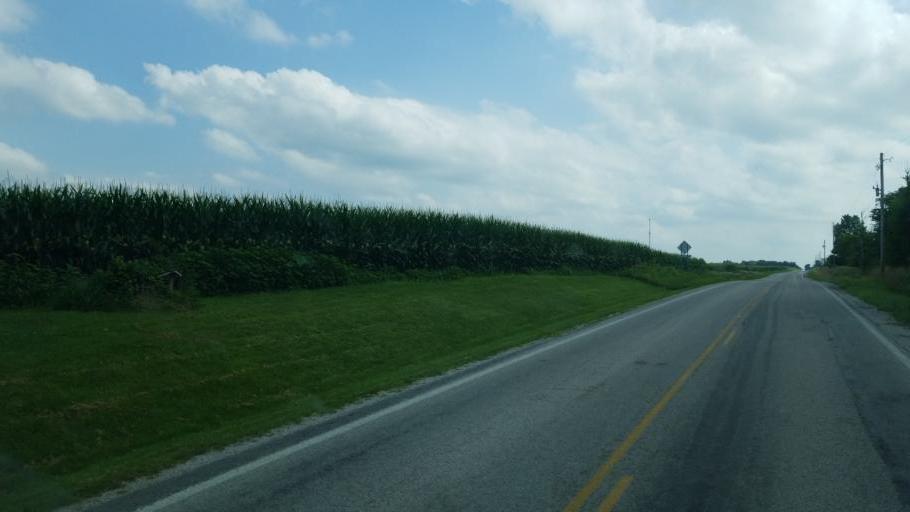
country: US
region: Ohio
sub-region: Crawford County
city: Crestline
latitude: 40.8486
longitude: -82.7817
